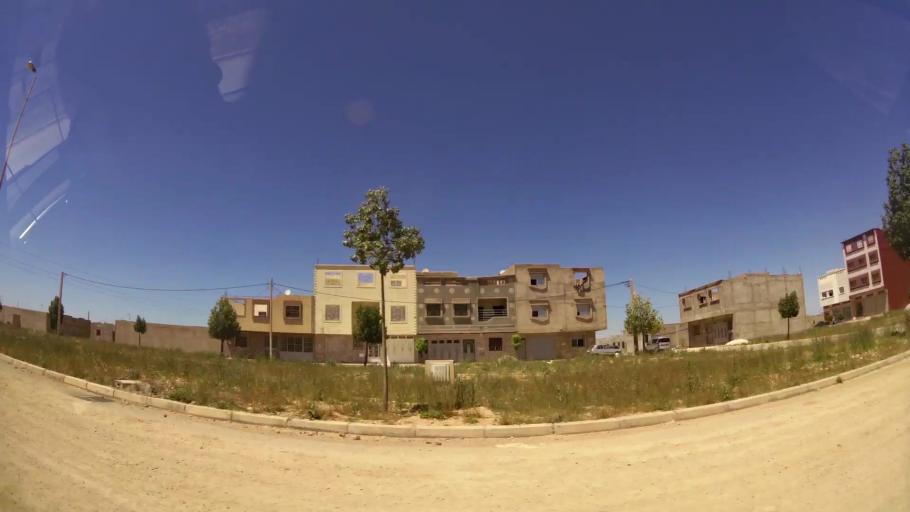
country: MA
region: Oriental
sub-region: Oujda-Angad
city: Oujda
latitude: 34.6815
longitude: -1.8569
